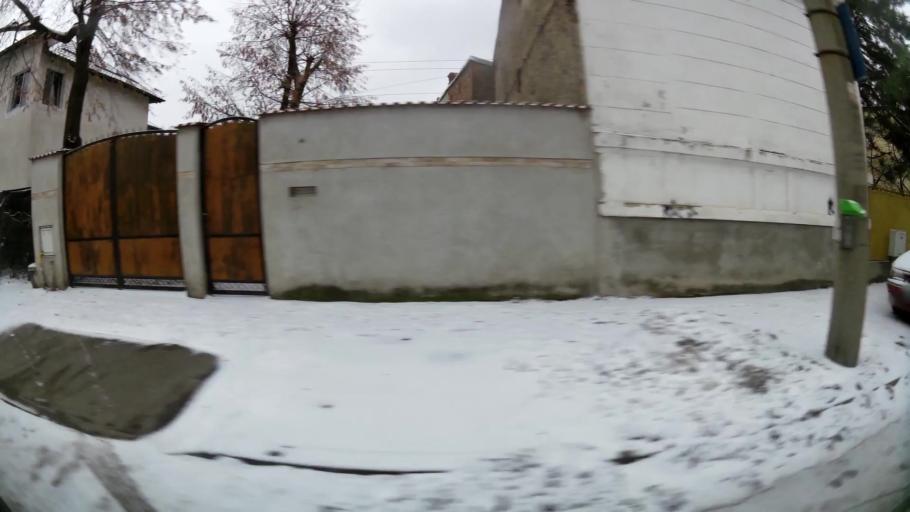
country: RO
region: Prahova
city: Ploiesti
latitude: 44.9362
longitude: 26.0373
